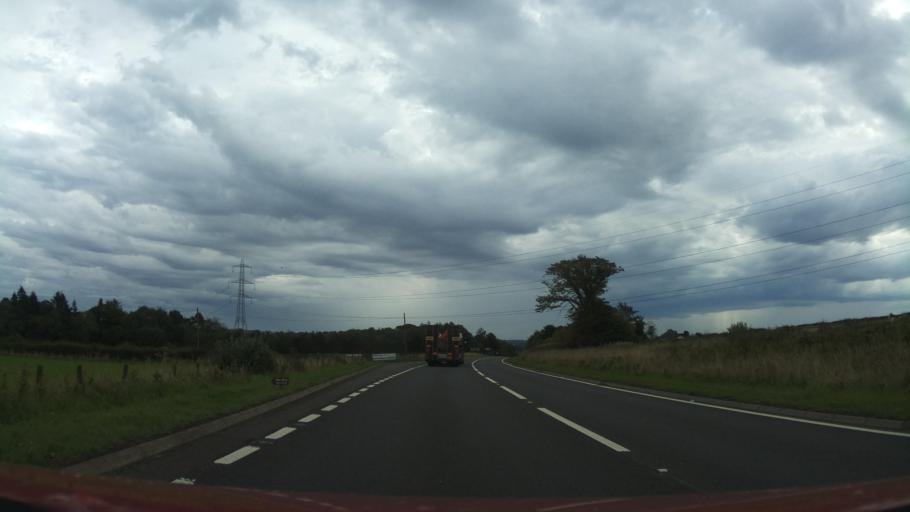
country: GB
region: Scotland
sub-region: Fife
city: High Valleyfield
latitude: 56.0665
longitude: -3.6248
